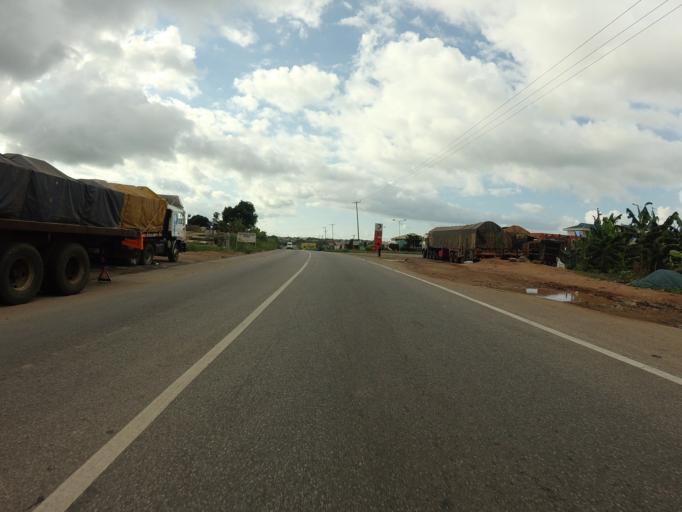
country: GH
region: Ashanti
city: Tafo
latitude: 6.8254
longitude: -1.6474
